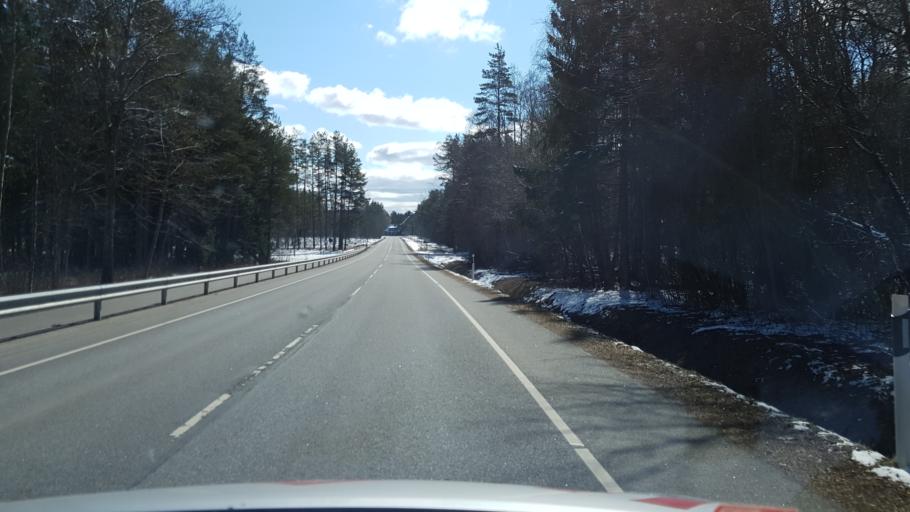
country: EE
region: Laeaene-Virumaa
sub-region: Kadrina vald
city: Kadrina
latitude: 59.4602
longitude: 26.0048
